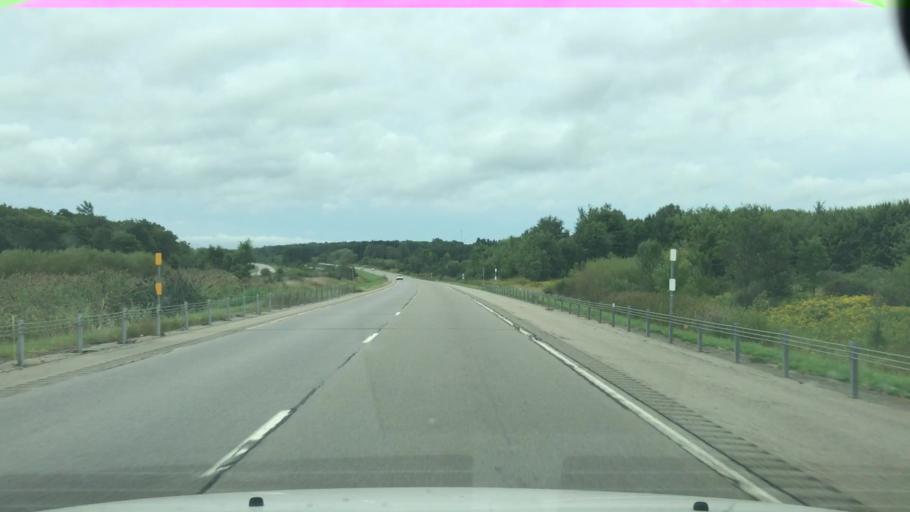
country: US
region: New York
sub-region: Erie County
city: North Boston
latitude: 42.6221
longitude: -78.7644
